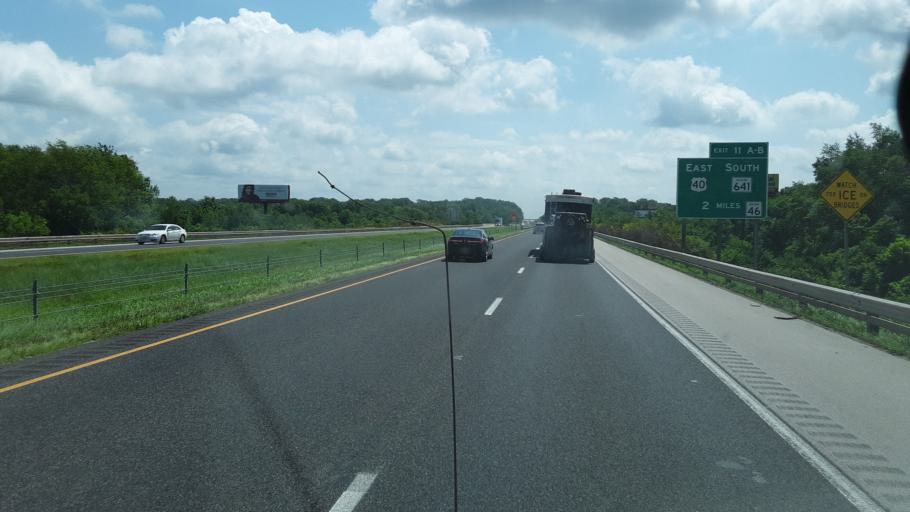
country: US
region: Indiana
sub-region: Vigo County
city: Terre Haute
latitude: 39.4307
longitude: -87.3826
